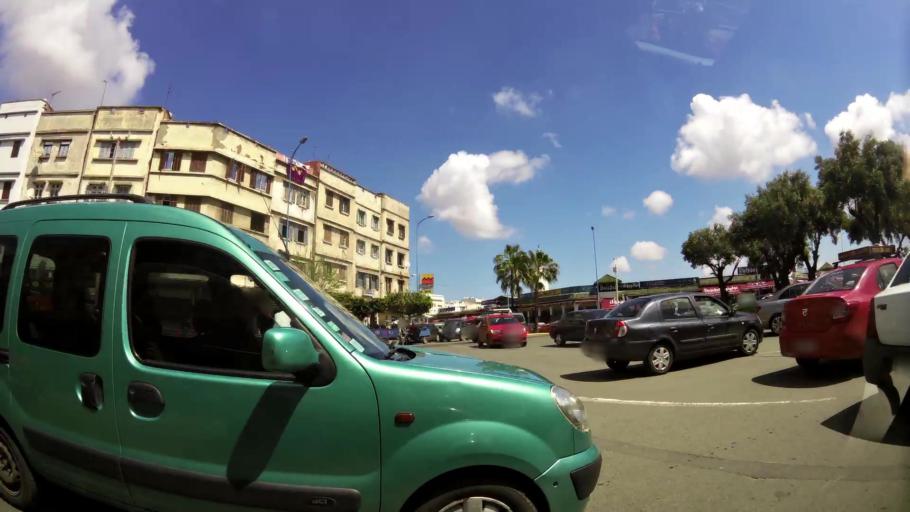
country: MA
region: Grand Casablanca
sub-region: Casablanca
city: Casablanca
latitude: 33.5619
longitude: -7.6011
